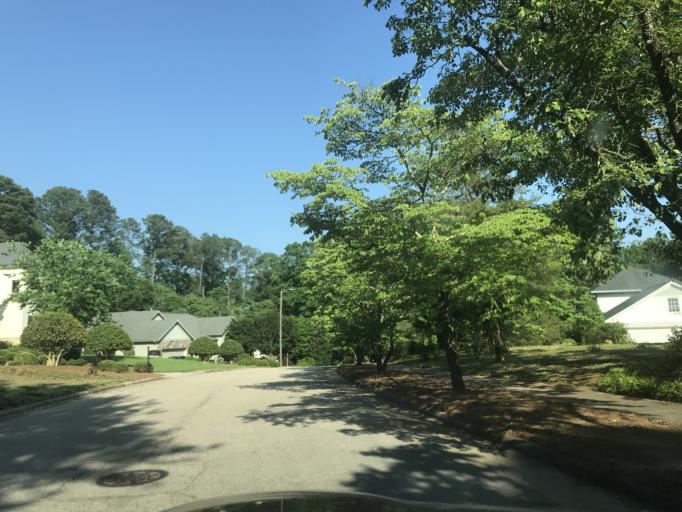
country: US
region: North Carolina
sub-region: Wake County
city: West Raleigh
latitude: 35.8732
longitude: -78.6100
